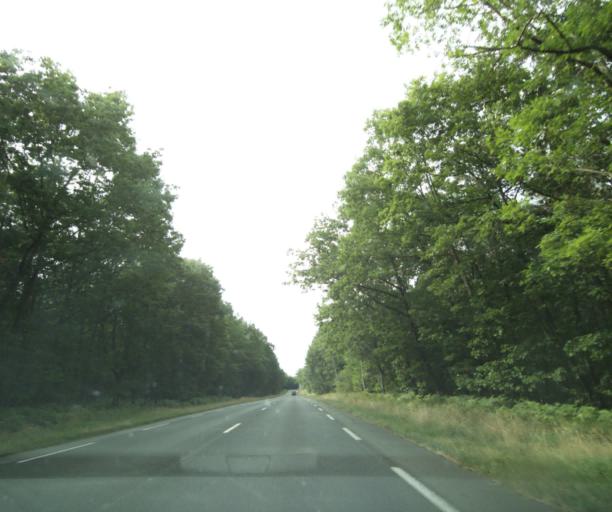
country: FR
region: Pays de la Loire
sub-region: Departement de la Sarthe
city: Marigne-Laille
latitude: 47.7690
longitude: 0.3501
